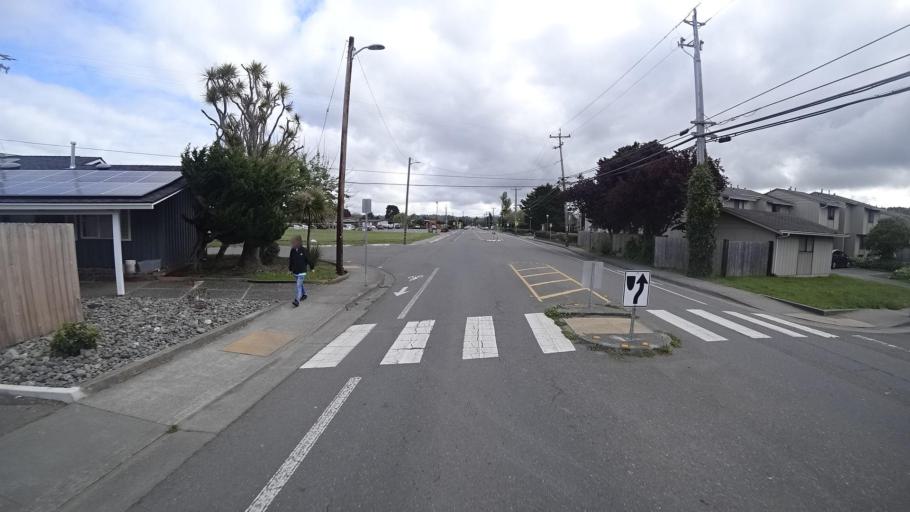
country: US
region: California
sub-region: Humboldt County
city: Arcata
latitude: 40.8832
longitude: -124.0909
